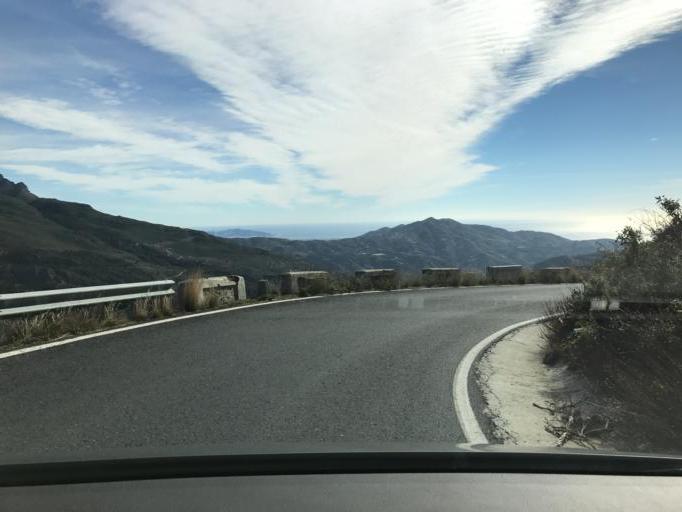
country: ES
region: Andalusia
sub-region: Provincia de Granada
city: Lentegi
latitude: 36.8344
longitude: -3.6981
